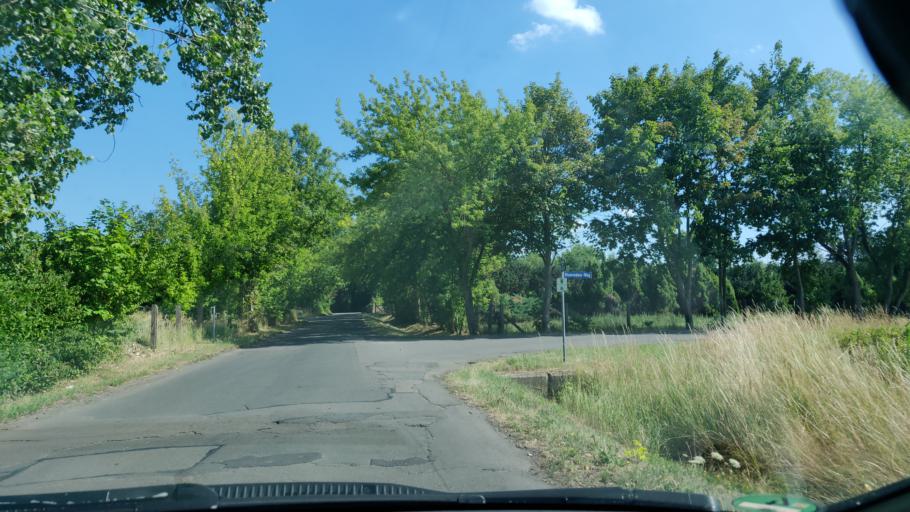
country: DE
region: Saxony
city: Borna
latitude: 51.0824
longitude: 12.5107
